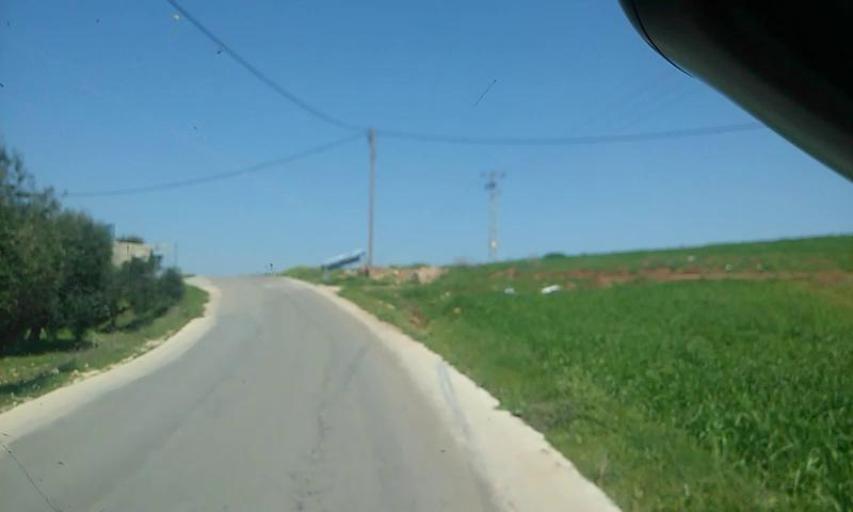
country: PS
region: West Bank
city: Al Majd
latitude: 31.4735
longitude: 34.9490
